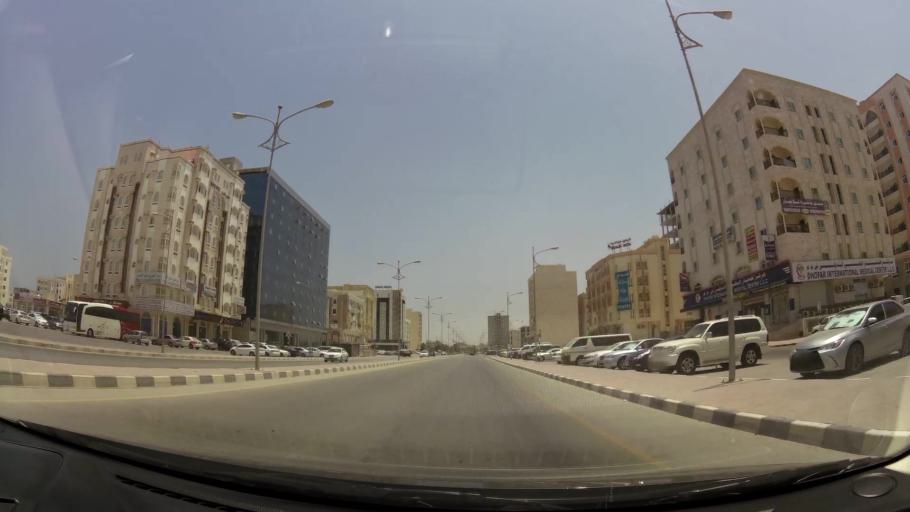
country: OM
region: Zufar
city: Salalah
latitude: 17.0194
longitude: 54.0983
